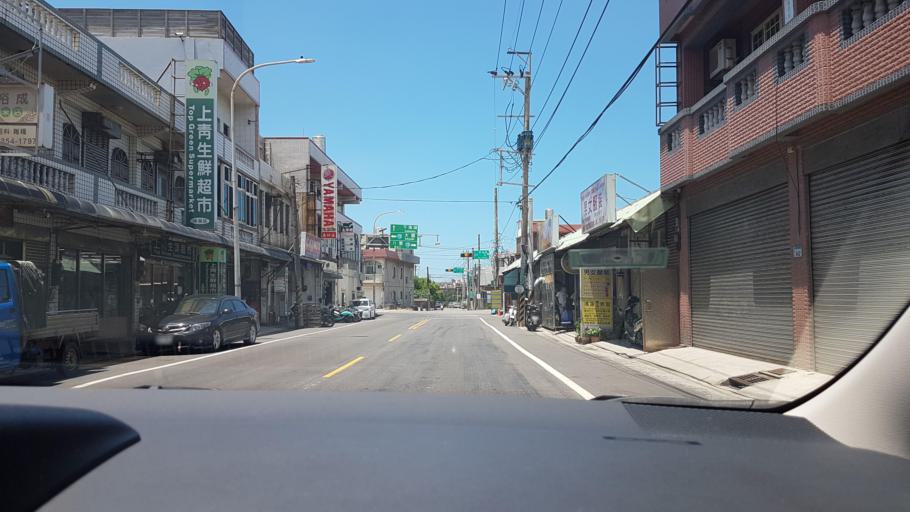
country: TW
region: Taiwan
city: Taoyuan City
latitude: 25.1111
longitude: 121.2545
